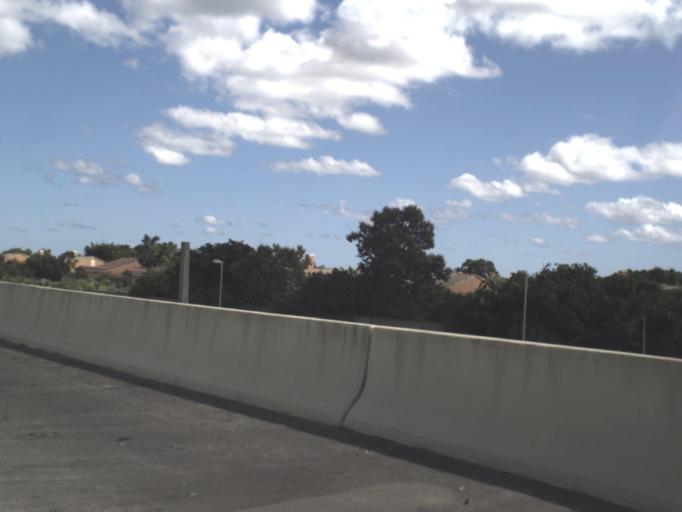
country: US
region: Florida
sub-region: Palm Beach County
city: Boca Pointe
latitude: 26.3009
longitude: -80.1867
